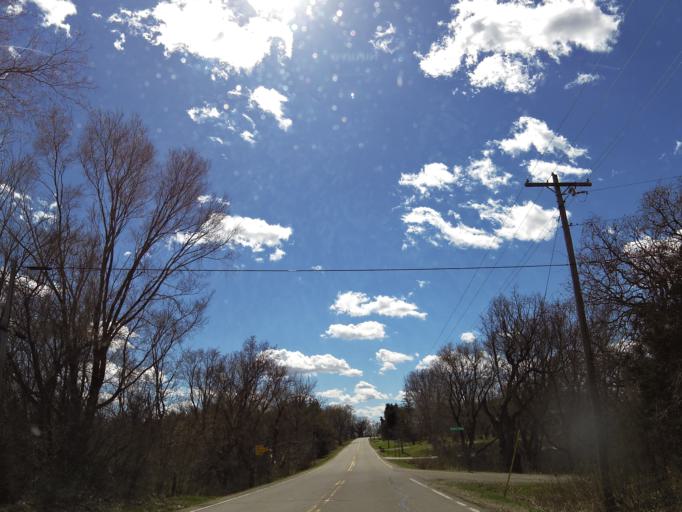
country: US
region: Minnesota
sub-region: Washington County
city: Cottage Grove
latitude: 44.7496
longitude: -92.9347
